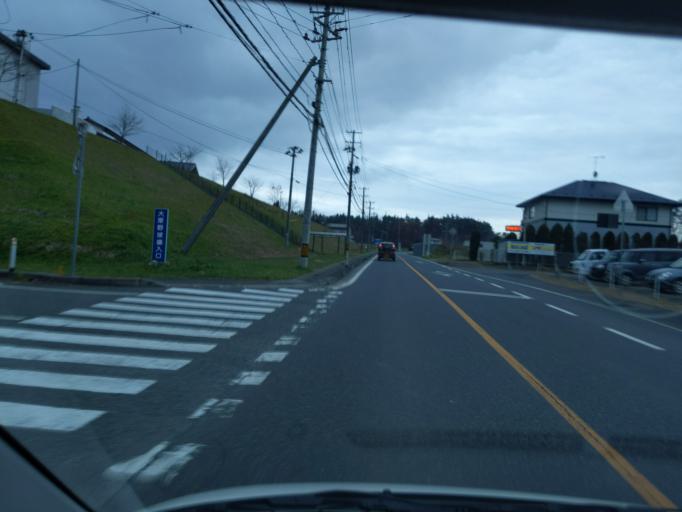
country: JP
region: Iwate
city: Ichinoseki
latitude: 39.0066
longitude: 141.3259
